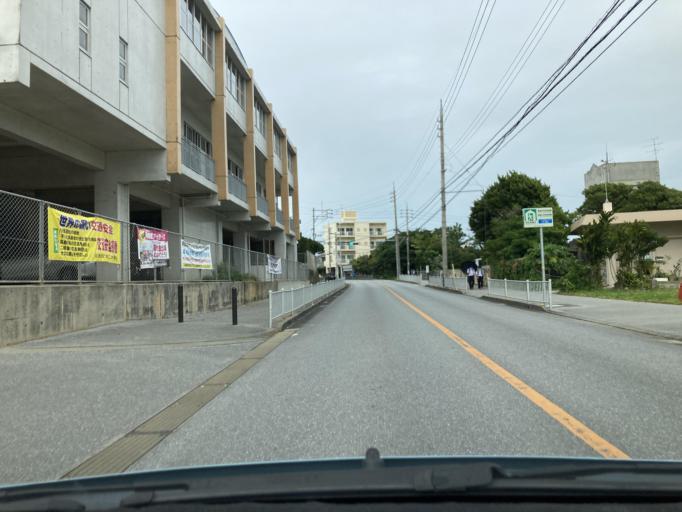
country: JP
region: Okinawa
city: Itoman
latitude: 26.1453
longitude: 127.6911
